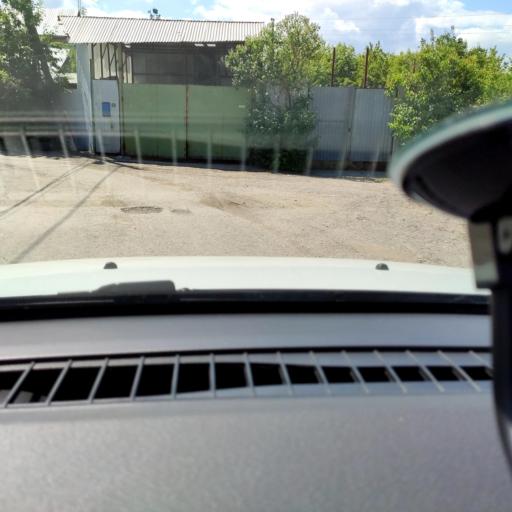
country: RU
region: Samara
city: Samara
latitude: 53.1751
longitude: 50.1629
